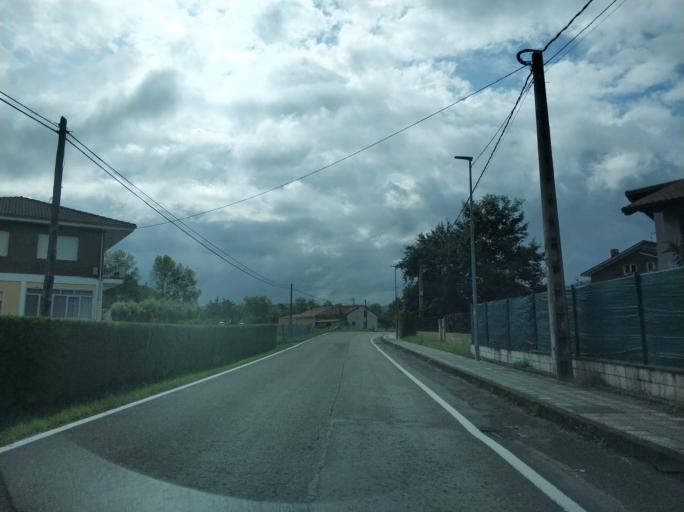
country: ES
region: Cantabria
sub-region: Provincia de Cantabria
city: Polanco
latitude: 43.3652
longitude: -3.9650
